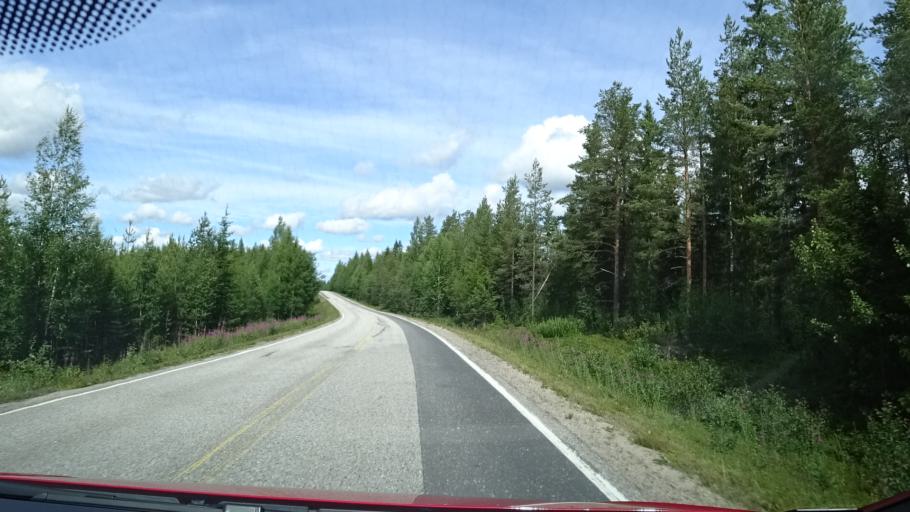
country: FI
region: Kainuu
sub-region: Kehys-Kainuu
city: Kuhmo
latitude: 64.4408
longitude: 29.8041
